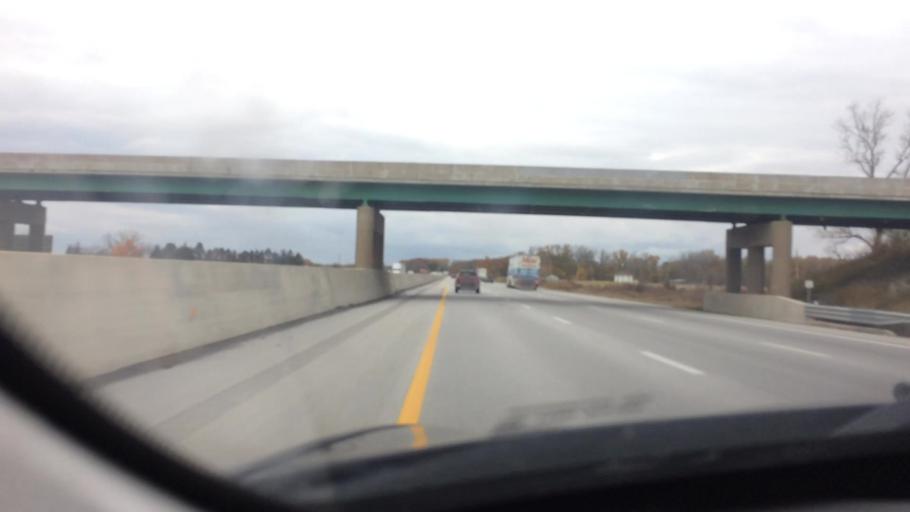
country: US
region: Ohio
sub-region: Wood County
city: North Baltimore
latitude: 41.2109
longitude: -83.6498
